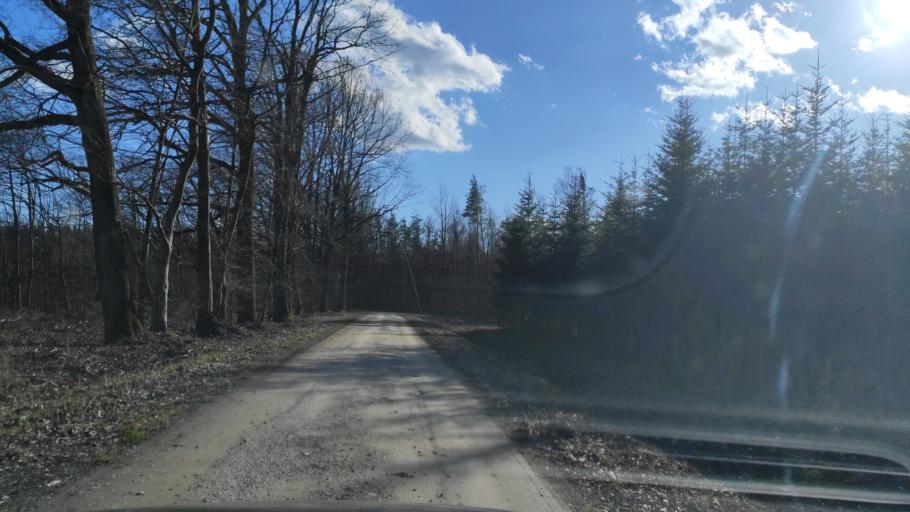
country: PL
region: Masovian Voivodeship
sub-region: Powiat radomski
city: Jedlnia-Letnisko
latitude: 51.4468
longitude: 21.2949
